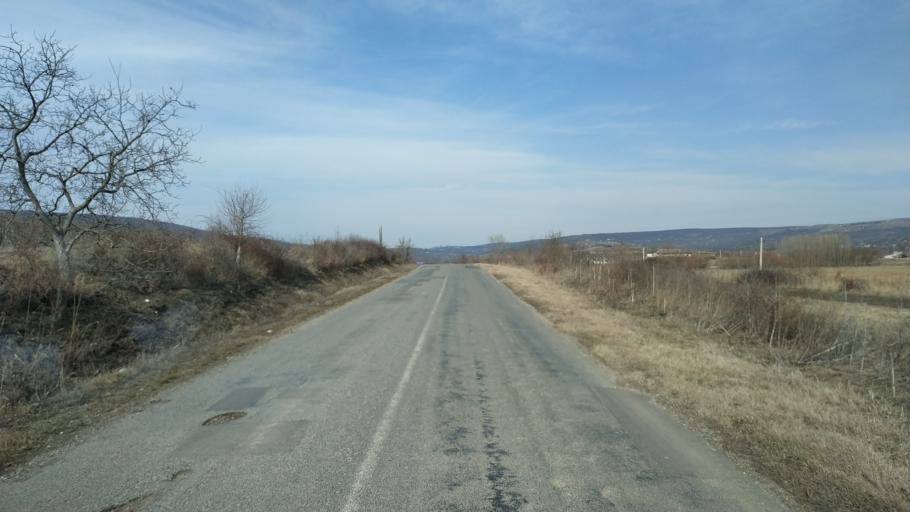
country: MD
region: Nisporeni
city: Nisporeni
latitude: 47.1649
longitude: 28.1003
